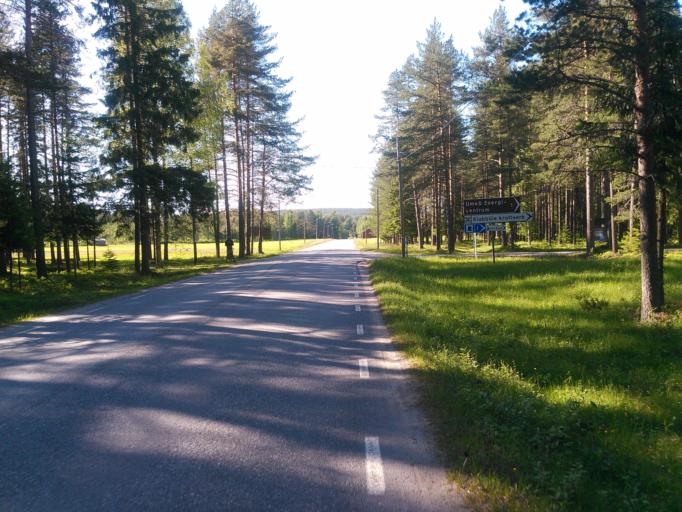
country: SE
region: Vaesterbotten
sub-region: Umea Kommun
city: Roback
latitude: 63.8319
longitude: 20.1099
